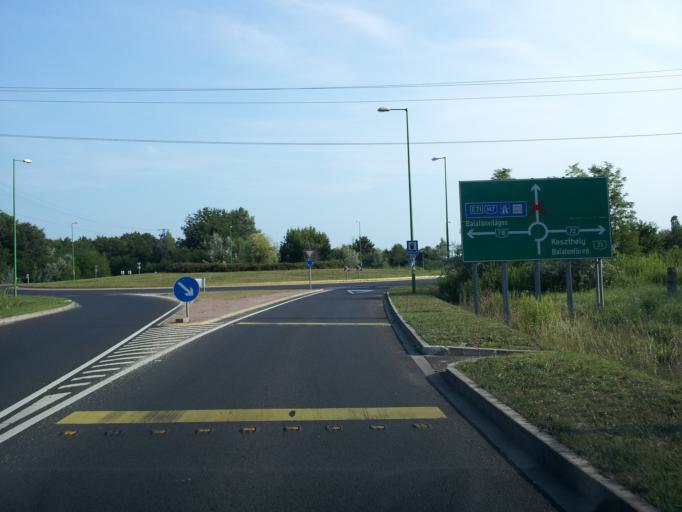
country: HU
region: Veszprem
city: Liter
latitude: 47.0742
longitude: 18.0355
